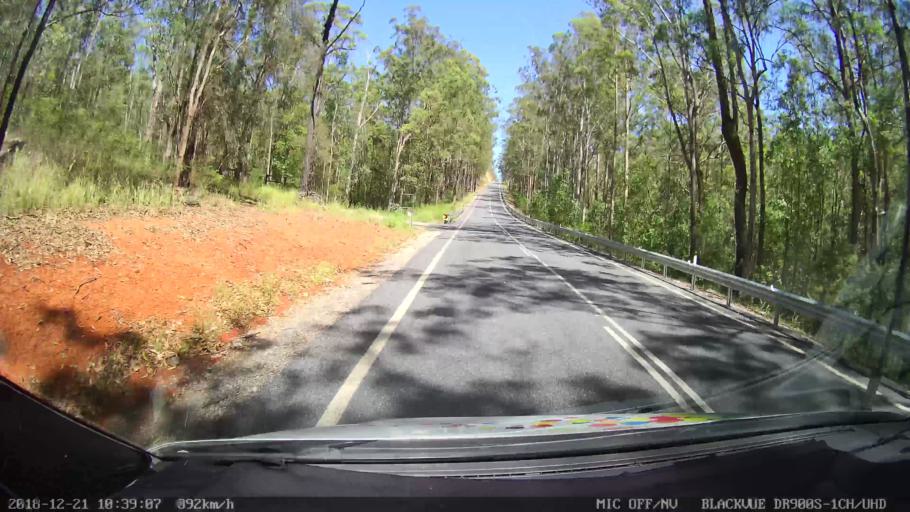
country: AU
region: New South Wales
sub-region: Clarence Valley
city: Gordon
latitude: -29.6100
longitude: 152.6009
